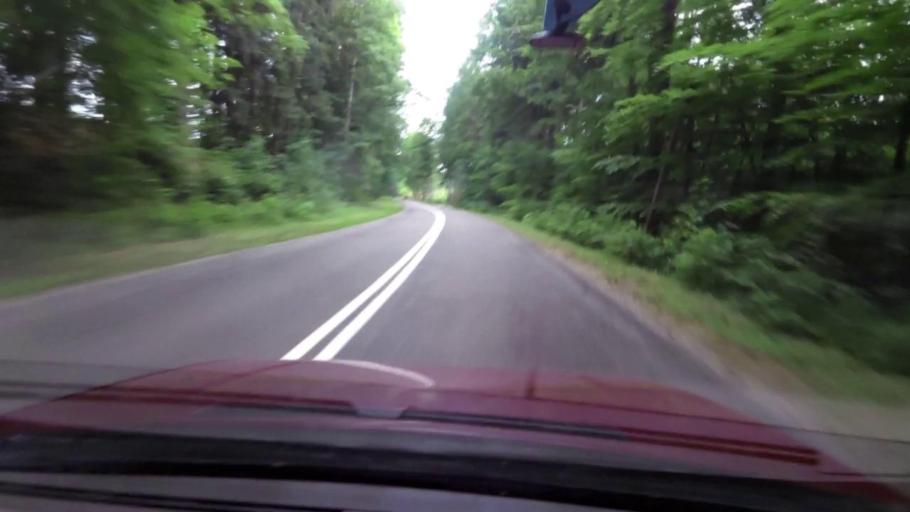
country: PL
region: West Pomeranian Voivodeship
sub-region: Powiat koszalinski
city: Sianow
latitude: 54.1873
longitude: 16.2654
